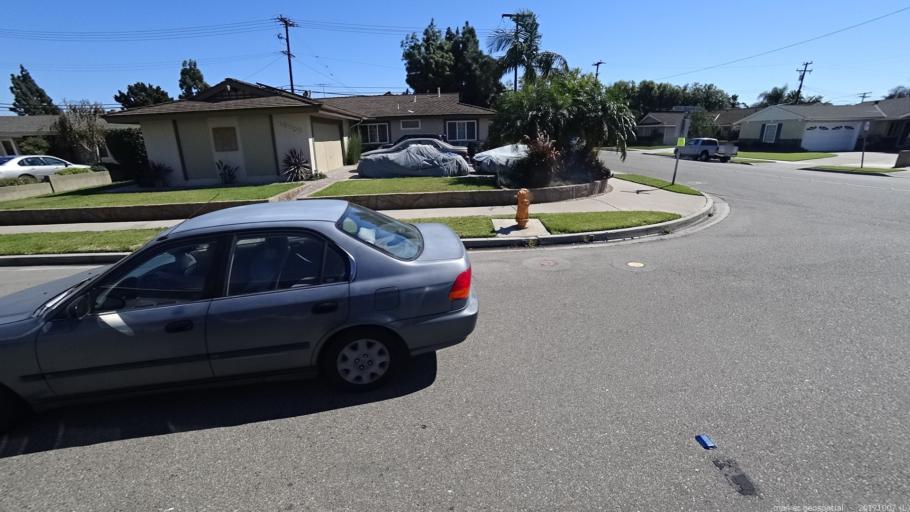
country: US
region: California
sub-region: Orange County
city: Westminster
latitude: 33.7781
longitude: -118.0362
